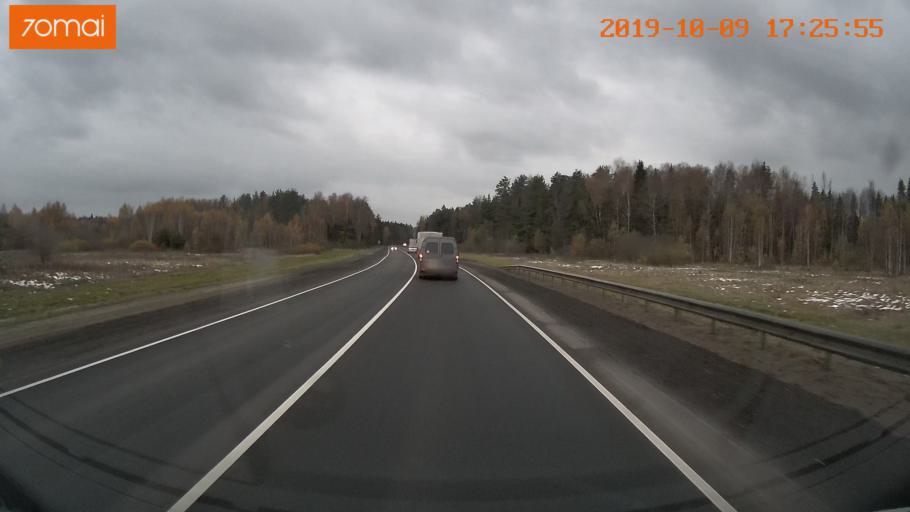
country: RU
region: Ivanovo
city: Furmanov
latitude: 57.1780
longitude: 41.0831
